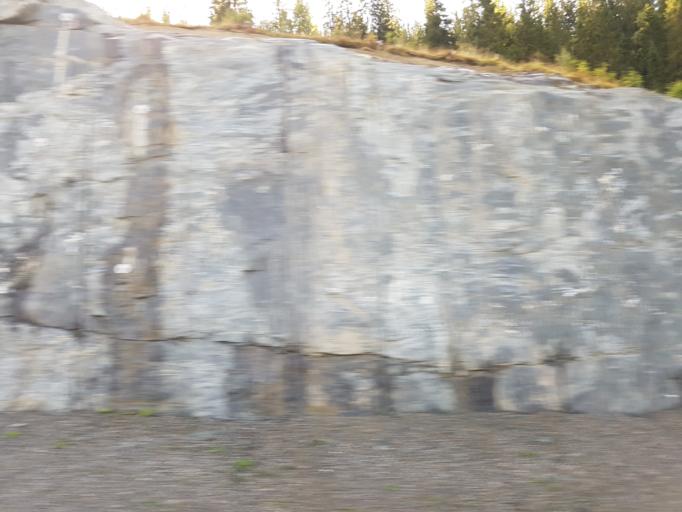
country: NO
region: Sor-Trondelag
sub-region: Rissa
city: Rissa
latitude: 63.6700
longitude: 10.2215
